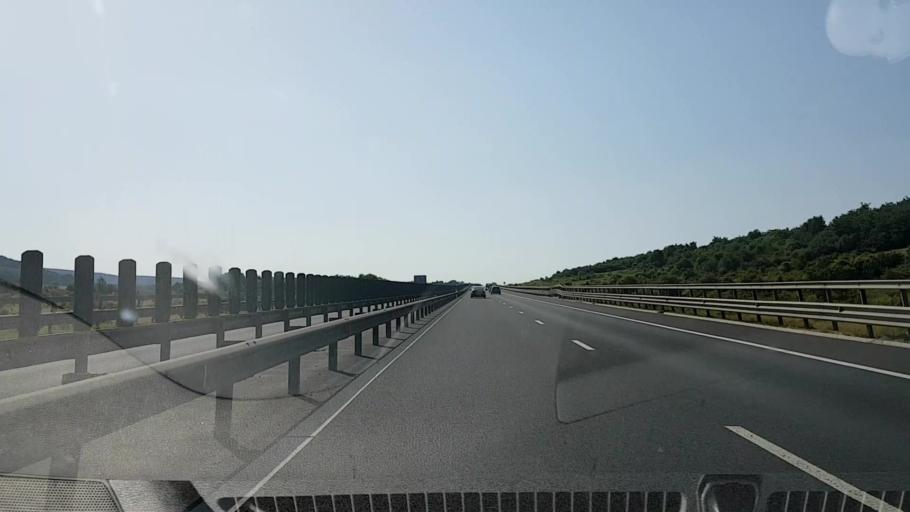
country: RO
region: Sibiu
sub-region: Oras Saliste
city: Saliste
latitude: 45.8118
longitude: 23.8949
